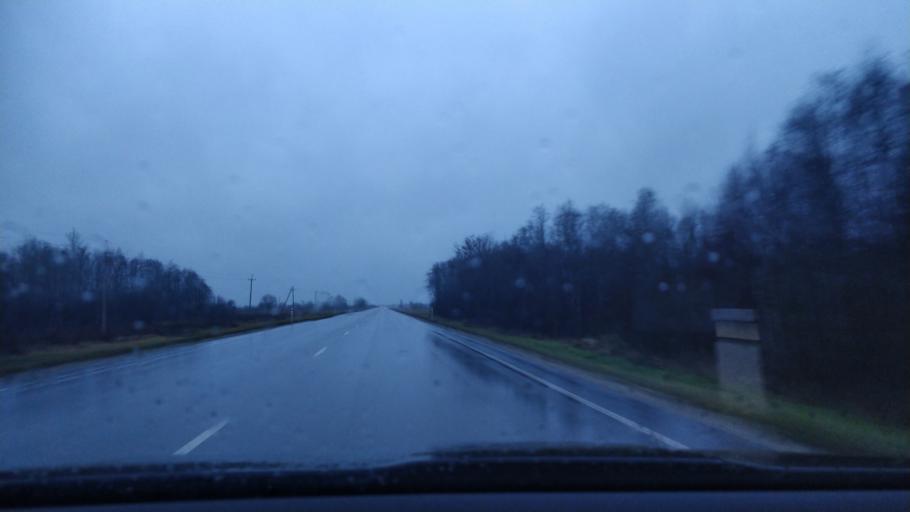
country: EE
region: Laeaene
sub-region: Lihula vald
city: Lihula
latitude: 58.7484
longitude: 23.9948
